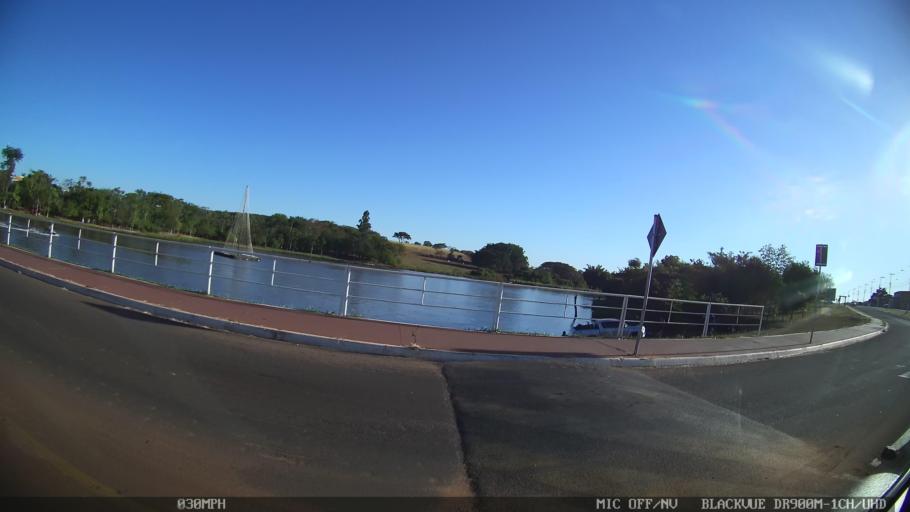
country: BR
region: Sao Paulo
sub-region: Guapiacu
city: Guapiacu
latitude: -20.7934
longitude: -49.2318
